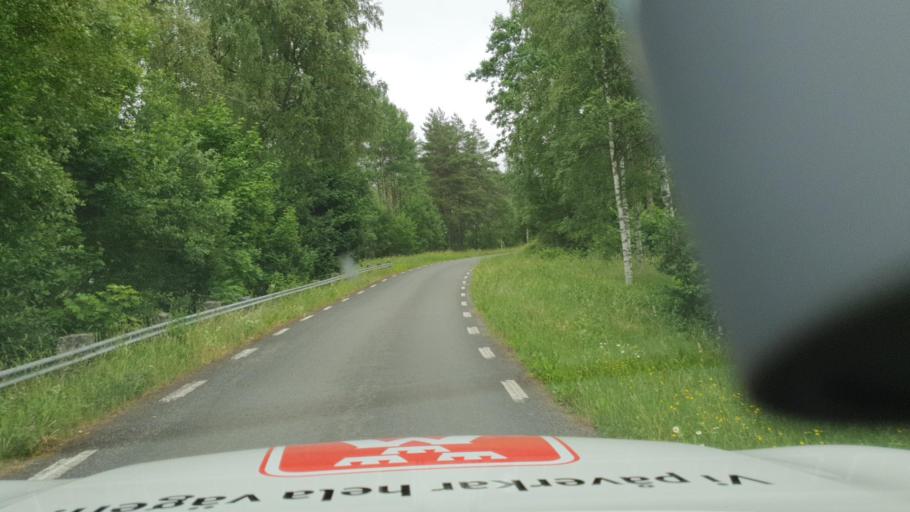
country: SE
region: Joenkoeping
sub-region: Mullsjo Kommun
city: Mullsjoe
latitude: 58.0572
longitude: 13.8005
